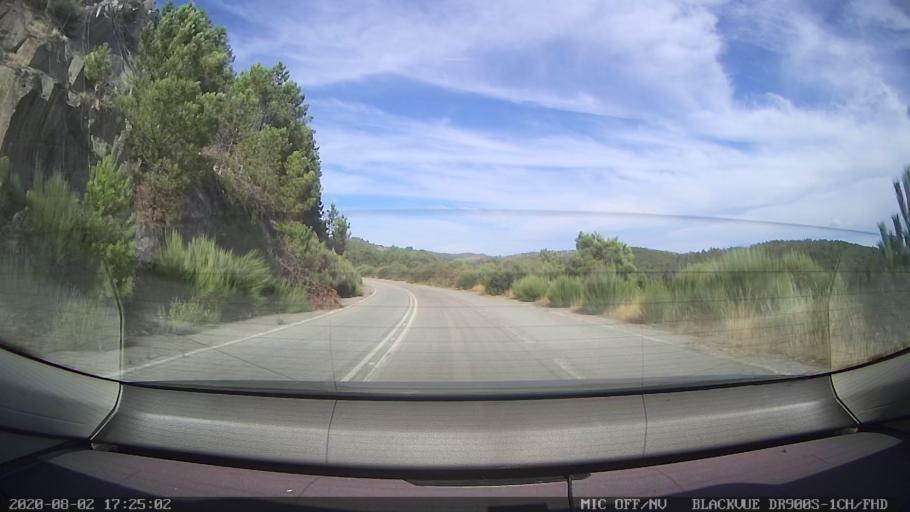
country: PT
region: Vila Real
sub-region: Sabrosa
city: Sabrosa
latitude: 41.3559
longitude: -7.5840
